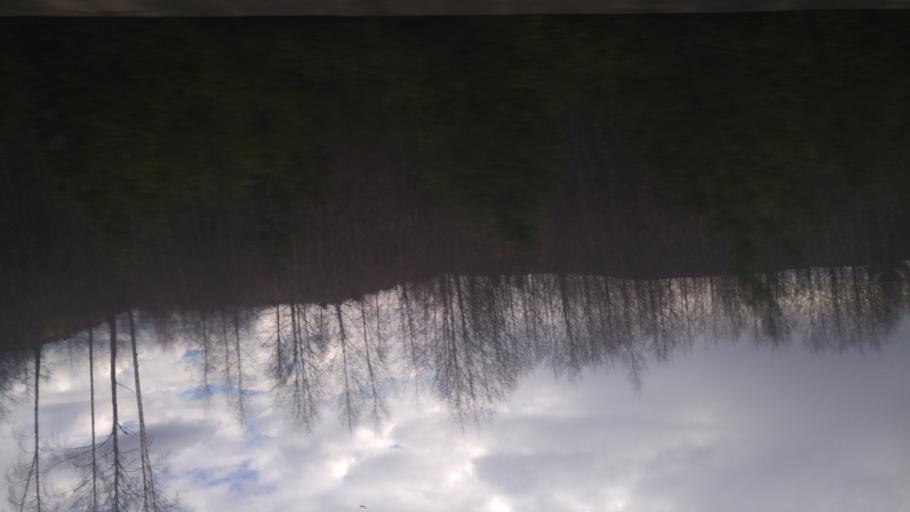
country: NO
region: Akershus
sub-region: Eidsvoll
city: Raholt
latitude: 60.2687
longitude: 11.1467
